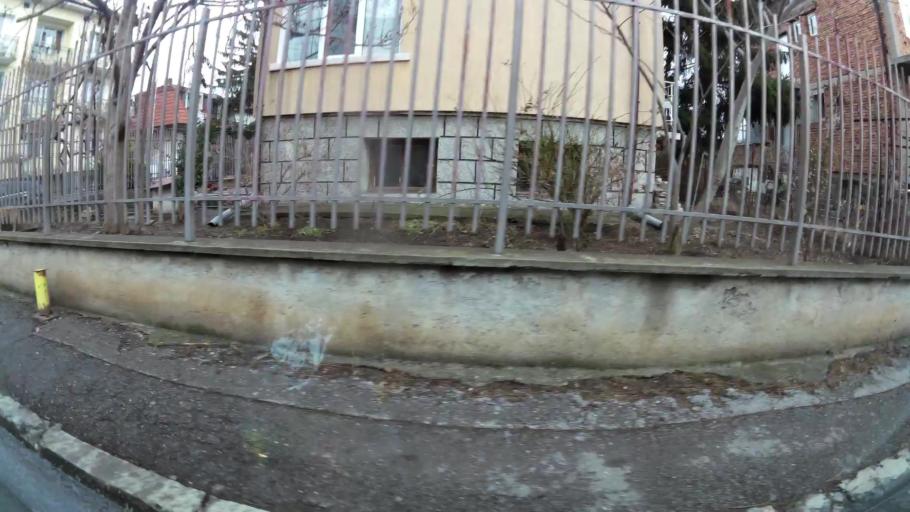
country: BG
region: Sofiya
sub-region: Obshtina Bozhurishte
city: Bozhurishte
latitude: 42.7437
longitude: 23.2663
